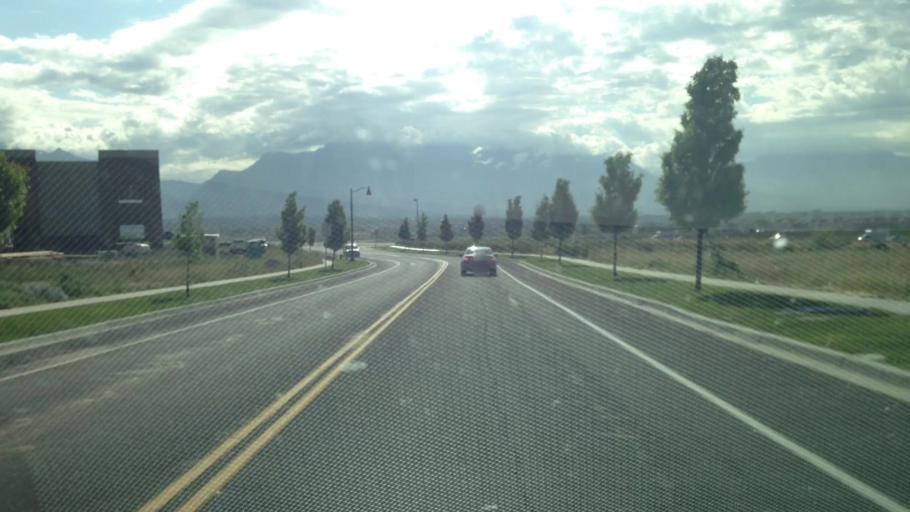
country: US
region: Utah
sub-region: Utah County
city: Saratoga Springs
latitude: 40.3948
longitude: -111.9203
